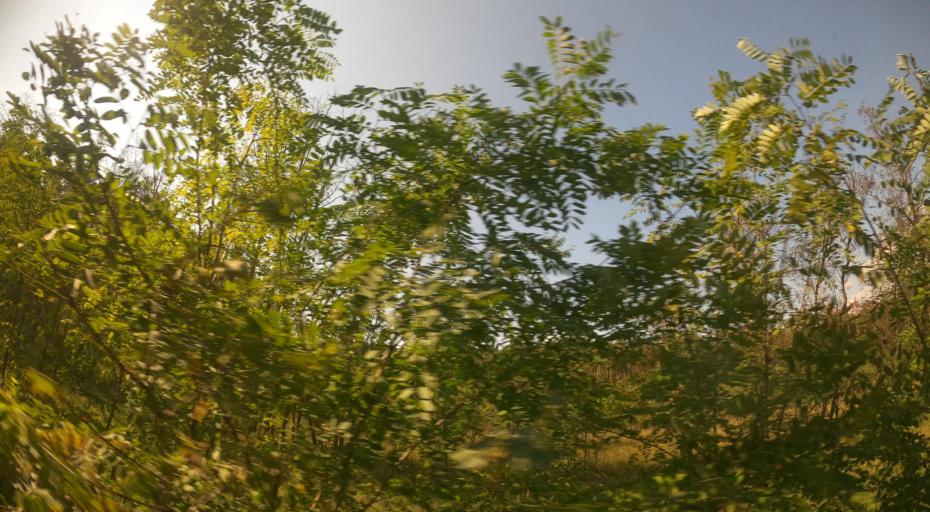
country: PL
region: Lubusz
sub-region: Powiat zielonogorski
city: Nowogrod Bobrzanski
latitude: 51.8379
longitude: 15.2612
